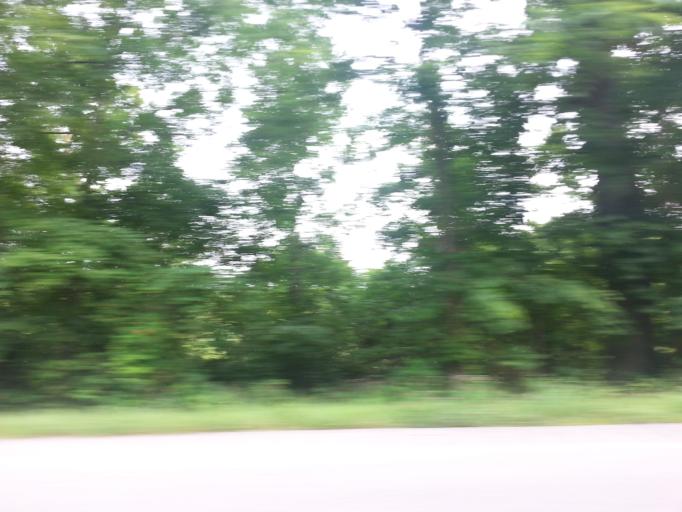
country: US
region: Kentucky
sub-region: Robertson County
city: Mount Olivet
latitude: 38.5115
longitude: -84.1514
